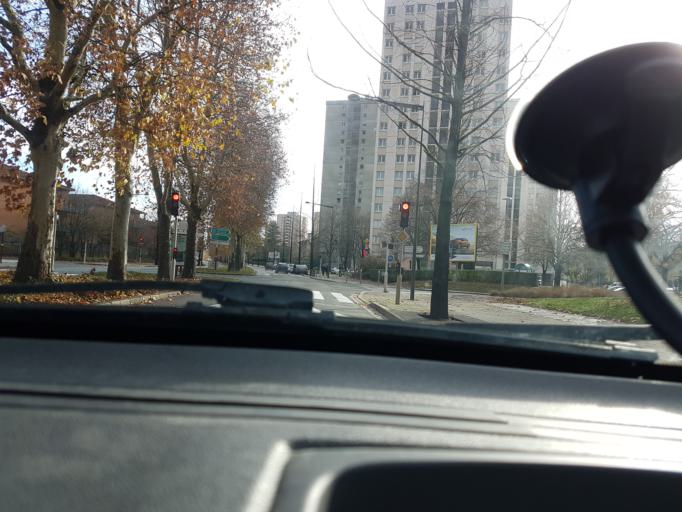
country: FR
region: Franche-Comte
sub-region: Territoire de Belfort
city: Bavilliers
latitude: 47.6339
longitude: 6.8387
